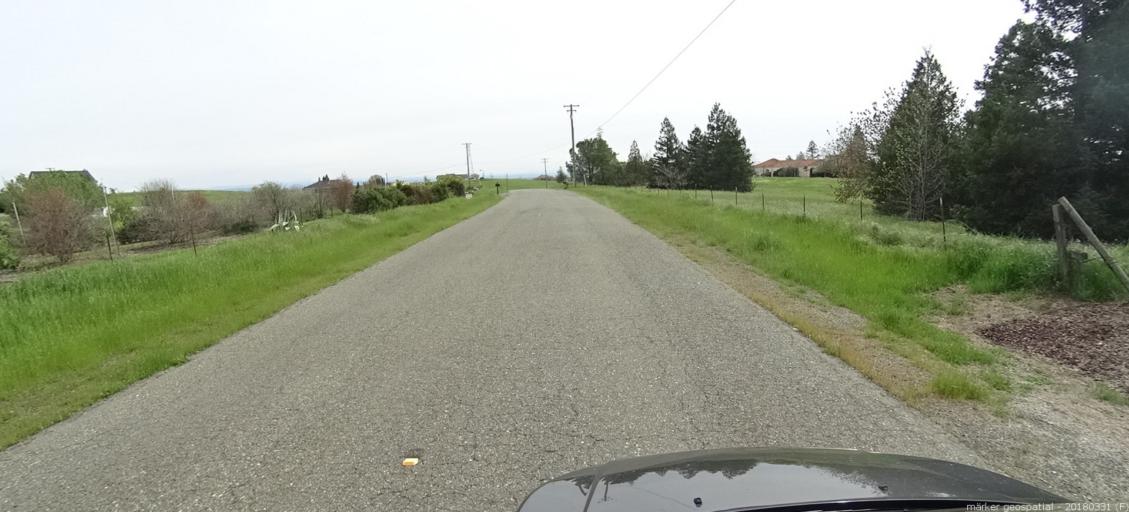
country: US
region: California
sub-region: Sacramento County
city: Rancho Murieta
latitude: 38.4918
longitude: -121.1466
